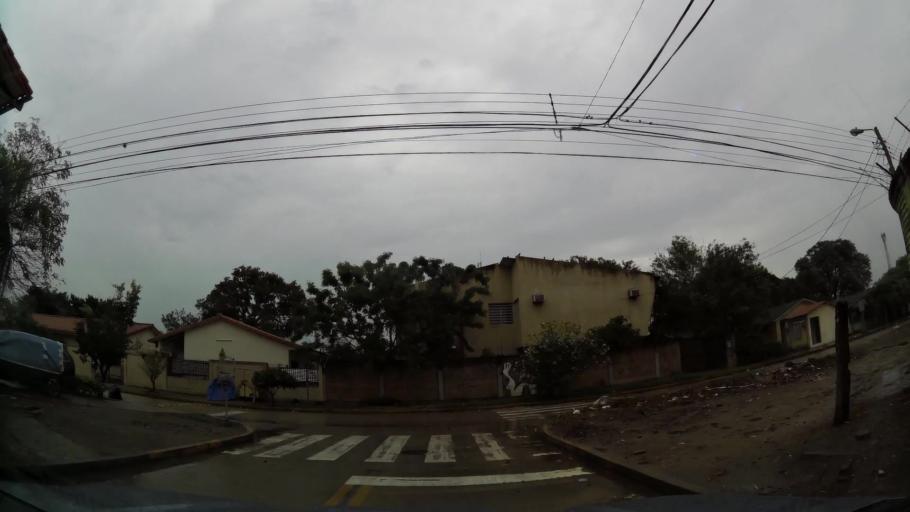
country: BO
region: Santa Cruz
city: Santa Cruz de la Sierra
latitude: -17.7899
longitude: -63.2115
